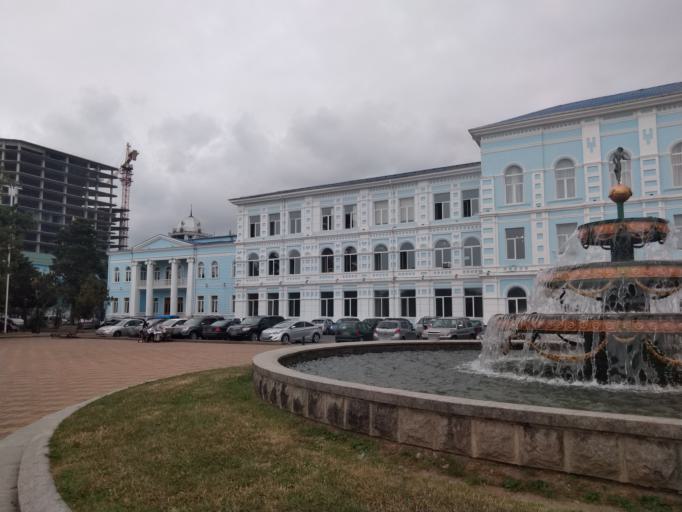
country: GE
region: Ajaria
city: Batumi
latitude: 41.6504
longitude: 41.6265
